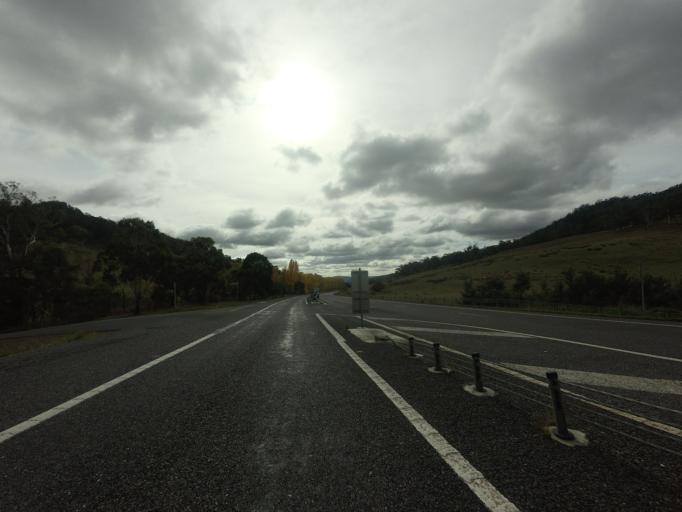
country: AU
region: Tasmania
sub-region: Brighton
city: Bridgewater
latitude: -42.5650
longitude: 147.2086
